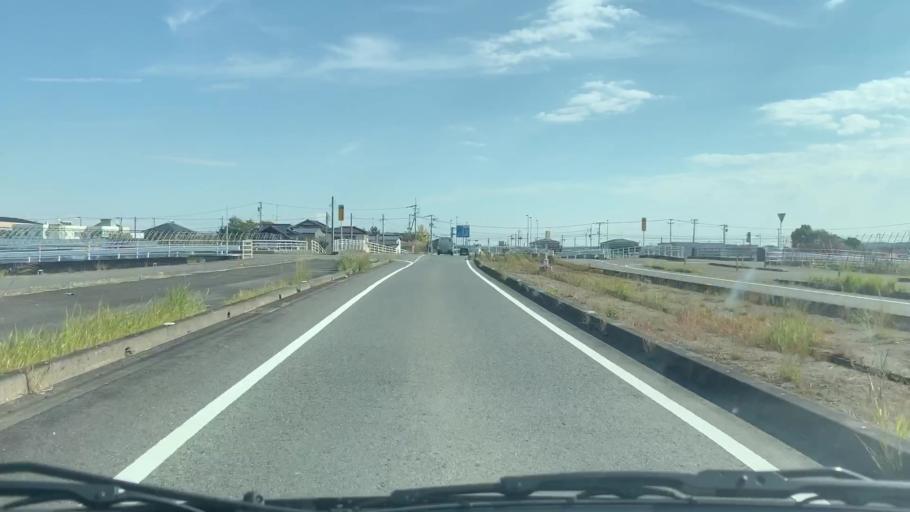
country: JP
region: Saga Prefecture
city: Saga-shi
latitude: 33.2213
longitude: 130.2061
